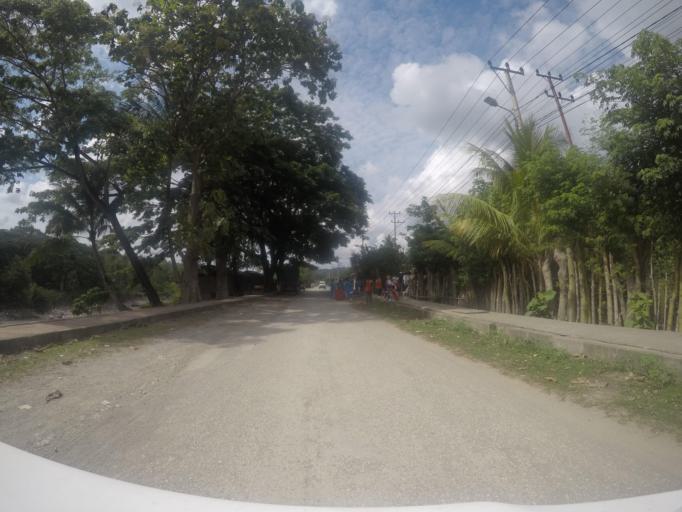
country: TL
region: Viqueque
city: Viqueque
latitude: -8.8572
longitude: 126.3657
